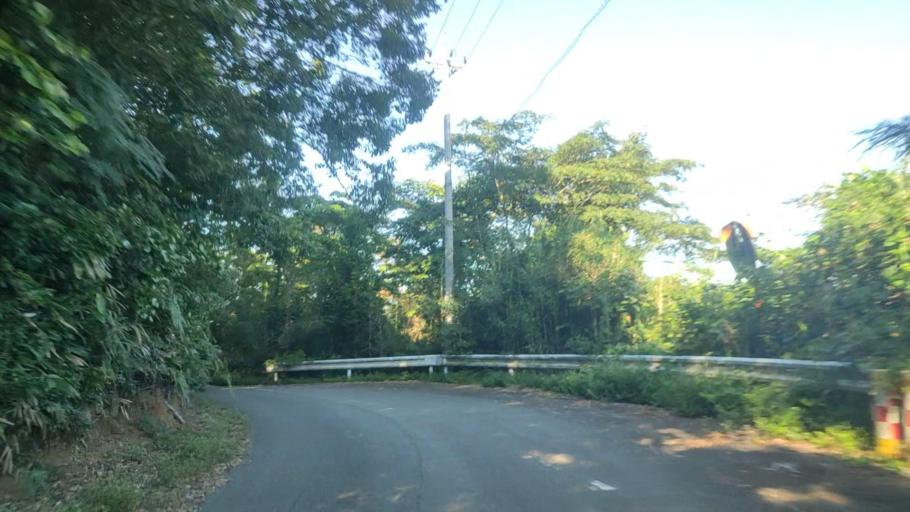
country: JP
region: Ishikawa
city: Nanao
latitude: 37.1244
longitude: 136.8956
